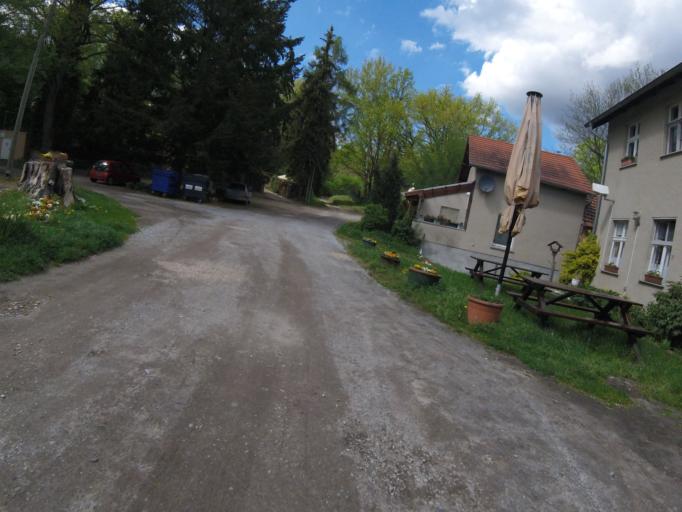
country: DE
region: Brandenburg
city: Teupitz
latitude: 52.1240
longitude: 13.5953
